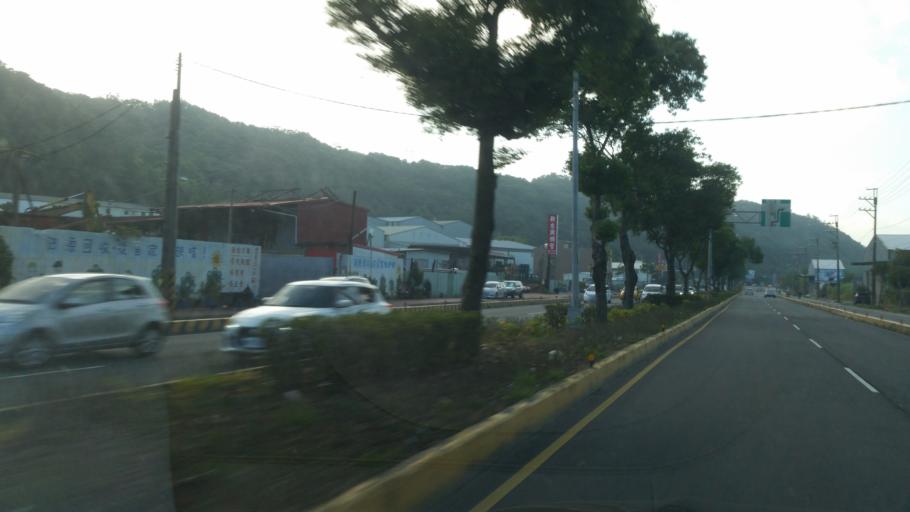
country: TW
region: Taiwan
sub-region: Taoyuan
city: Taoyuan
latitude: 25.0158
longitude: 121.3481
